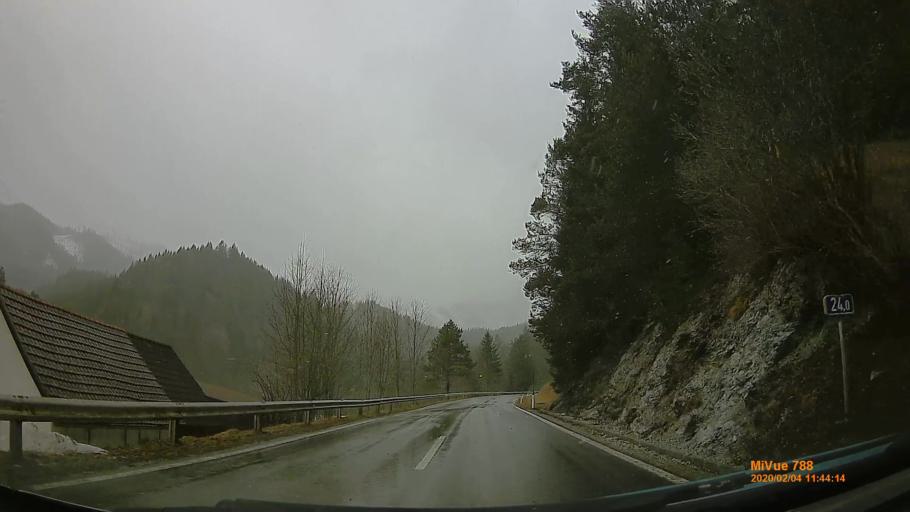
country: AT
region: Styria
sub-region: Politischer Bezirk Bruck-Muerzzuschlag
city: Muerzsteg
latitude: 47.6857
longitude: 15.4824
